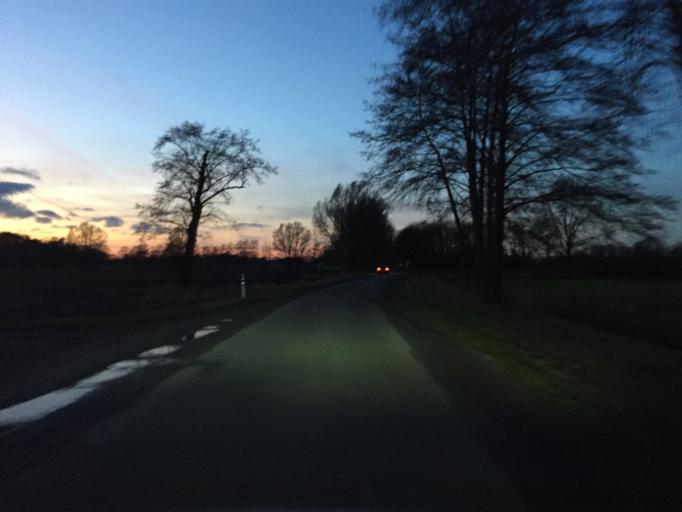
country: DE
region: Lower Saxony
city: Kirchdorf
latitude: 52.6298
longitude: 8.8712
